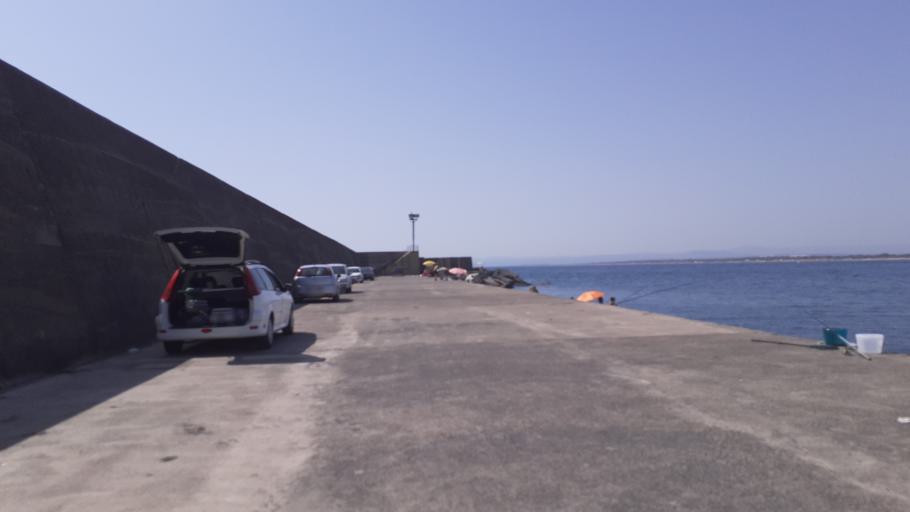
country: IT
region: Sicily
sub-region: Catania
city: Catania
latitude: 37.4853
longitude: 15.0994
